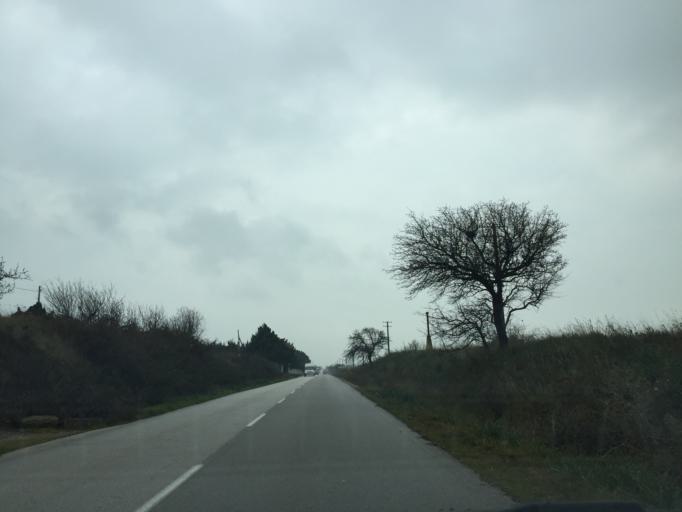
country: IT
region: Apulia
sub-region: Provincia di Foggia
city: Castelluccio dei Sauri
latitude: 41.4084
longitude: 15.4454
